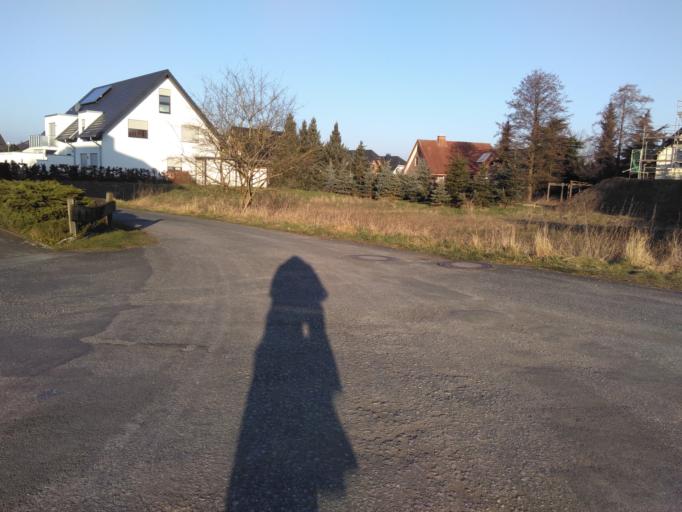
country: DE
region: North Rhine-Westphalia
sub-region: Regierungsbezirk Detmold
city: Verl
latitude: 51.8841
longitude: 8.4956
